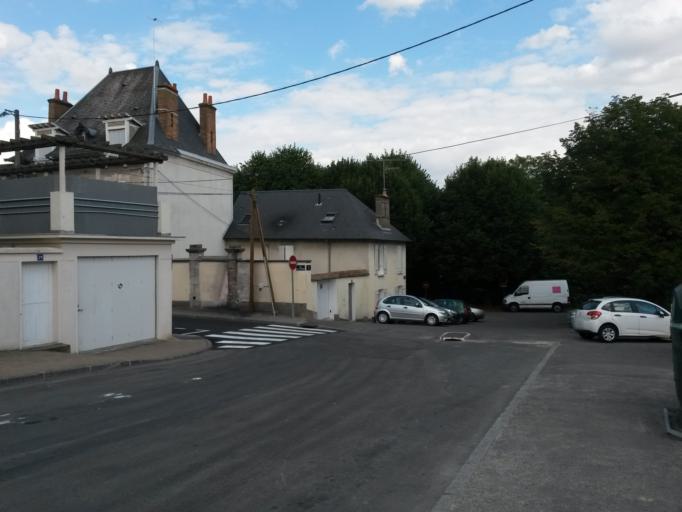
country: FR
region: Centre
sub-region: Departement du Loiret
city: Pithiviers
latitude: 48.1711
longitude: 2.2570
